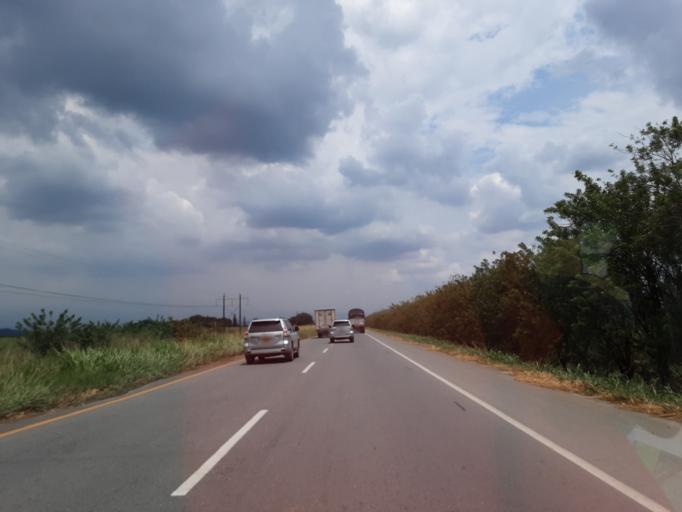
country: CO
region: Cauca
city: Caloto
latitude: 3.1118
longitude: -76.4669
